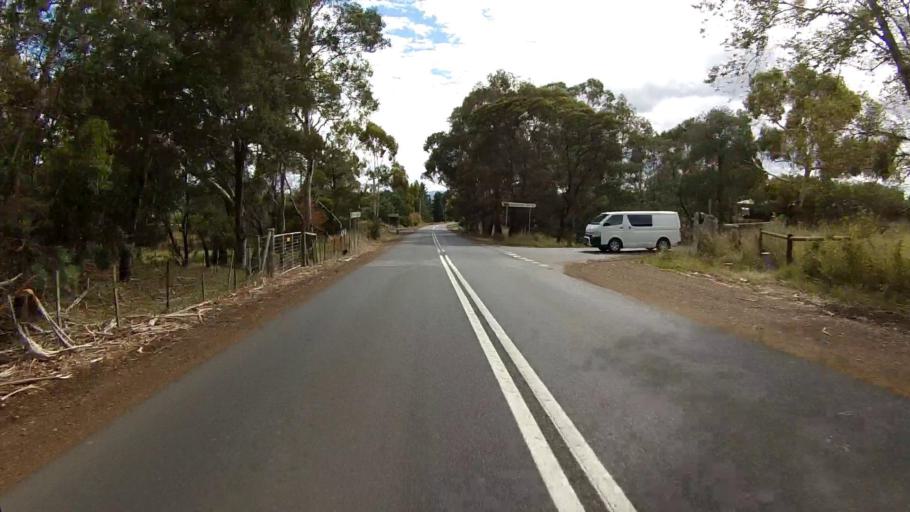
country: AU
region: Tasmania
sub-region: Clarence
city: Lindisfarne
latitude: -42.7654
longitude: 147.3927
